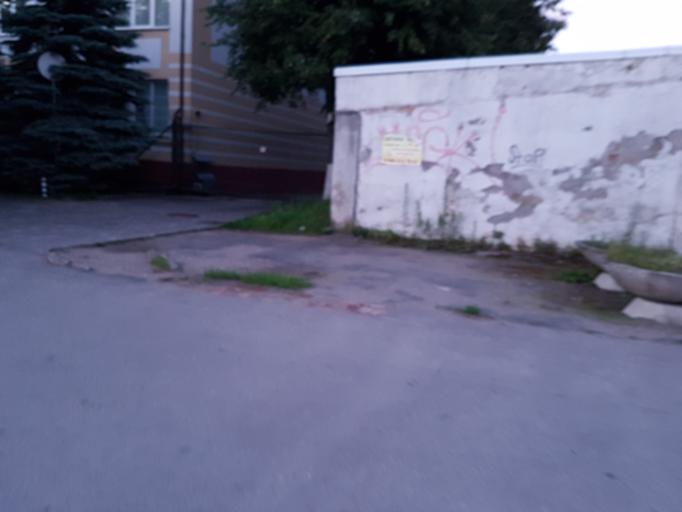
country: RU
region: Kaliningrad
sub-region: Gorod Kaliningrad
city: Kaliningrad
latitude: 54.6889
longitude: 20.5234
